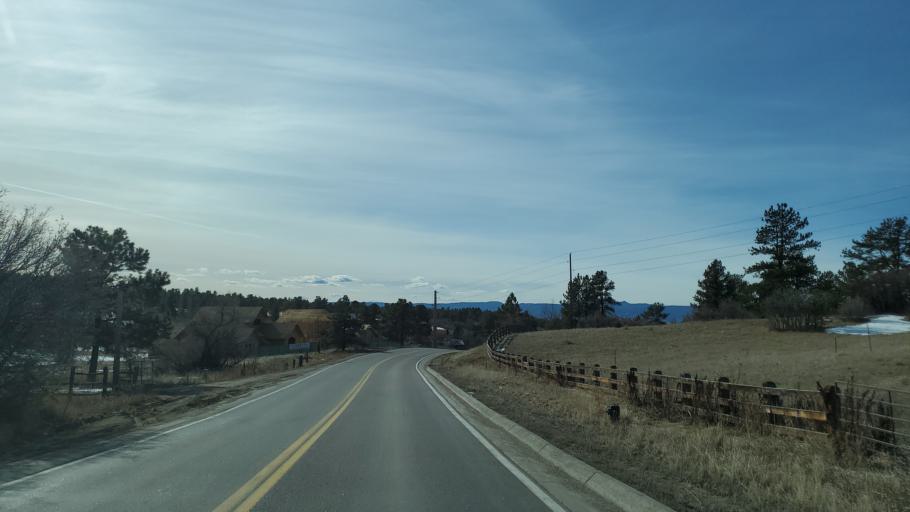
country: US
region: Colorado
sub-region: Douglas County
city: Castle Pines
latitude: 39.4469
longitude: -104.8782
